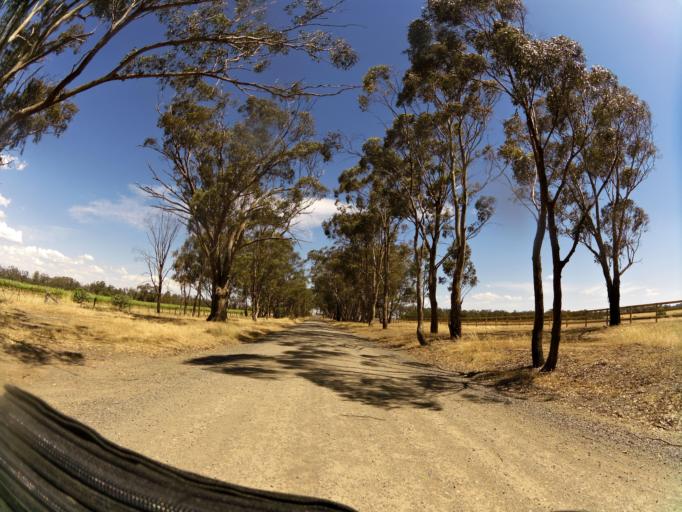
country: AU
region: Victoria
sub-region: Campaspe
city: Kyabram
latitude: -36.8355
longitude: 145.0744
